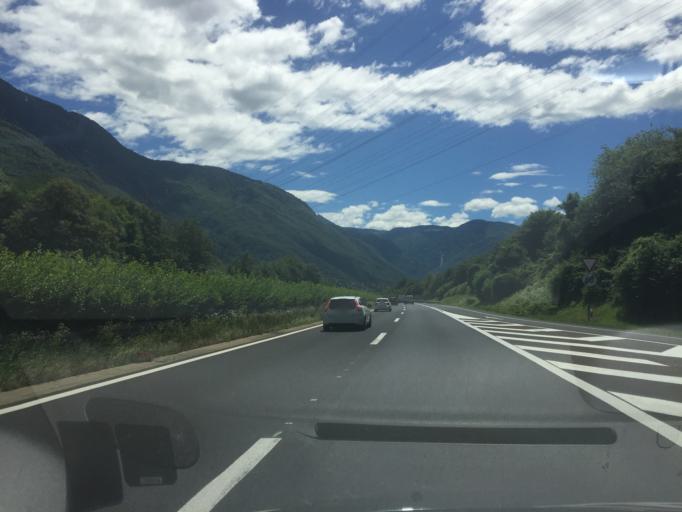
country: CH
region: Ticino
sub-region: Riviera District
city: Claro
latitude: 46.2726
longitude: 8.9992
